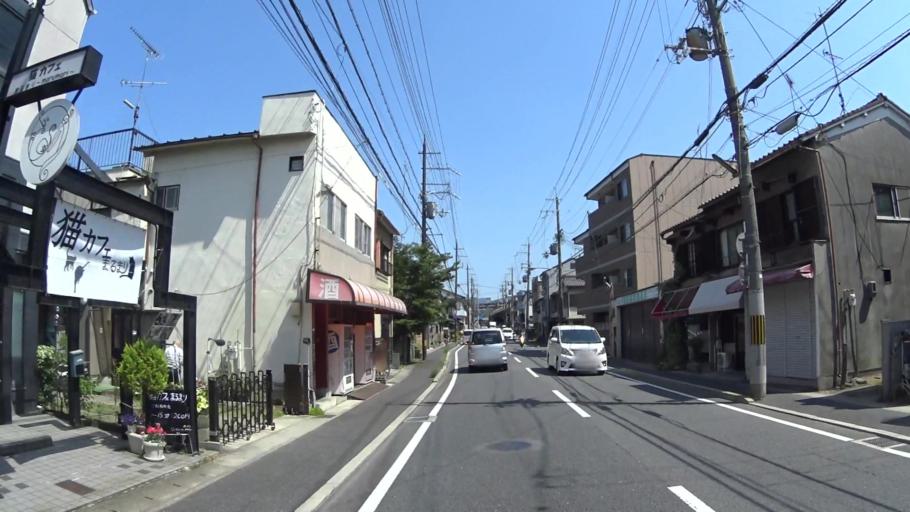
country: JP
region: Kyoto
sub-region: Kyoto-shi
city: Kamigyo-ku
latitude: 35.0548
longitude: 135.7914
